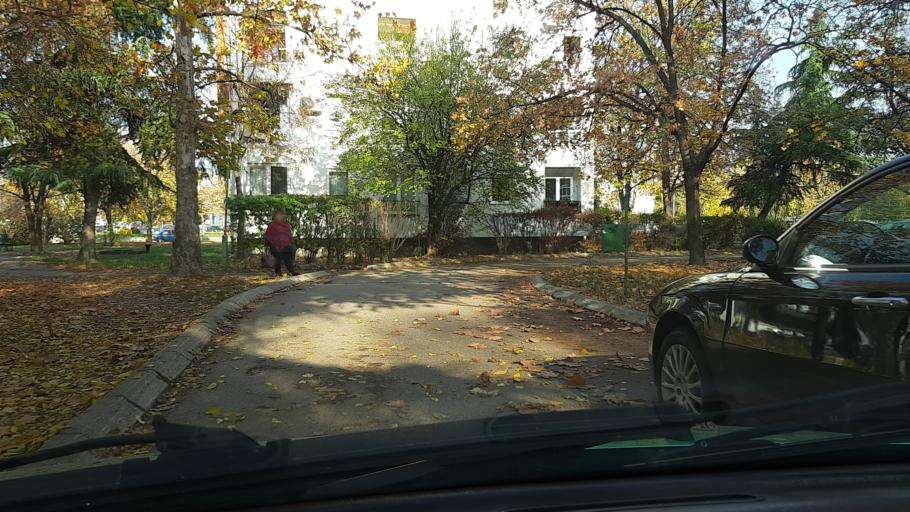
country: MK
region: Karpos
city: Skopje
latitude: 41.9882
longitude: 21.4592
